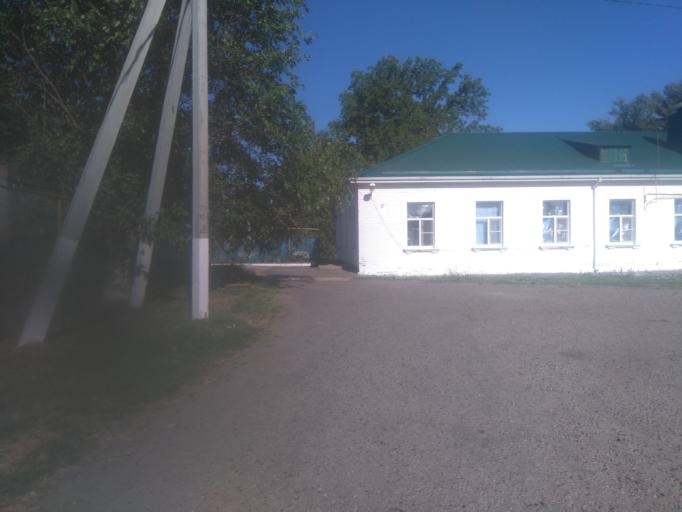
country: RU
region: Krasnodarskiy
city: Fastovetskaya
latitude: 45.9119
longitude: 40.1537
